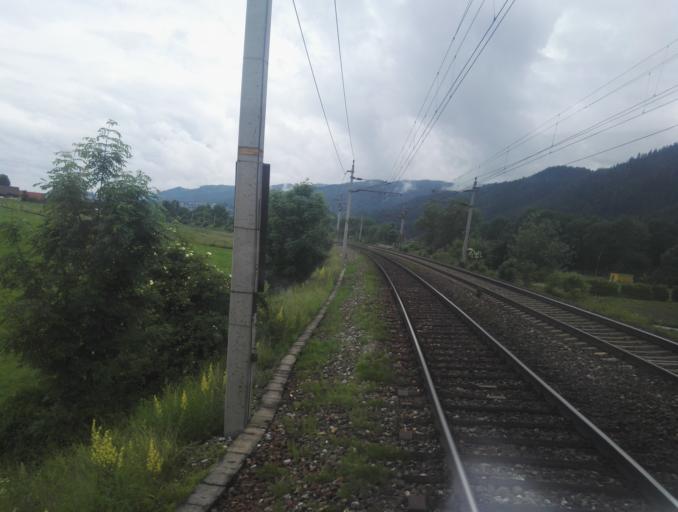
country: AT
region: Styria
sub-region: Politischer Bezirk Bruck-Muerzzuschlag
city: Krieglach
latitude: 47.5477
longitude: 15.5373
